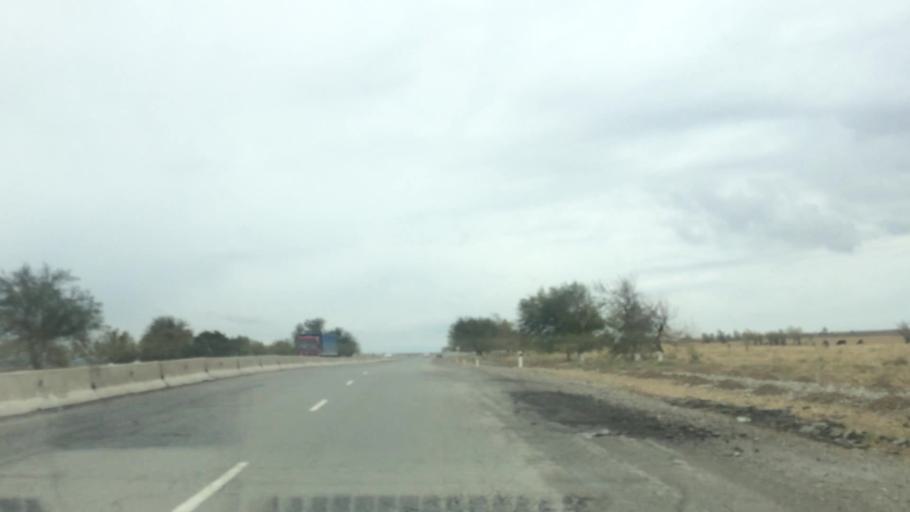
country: UZ
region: Samarqand
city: Bulung'ur
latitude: 39.8393
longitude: 67.4480
